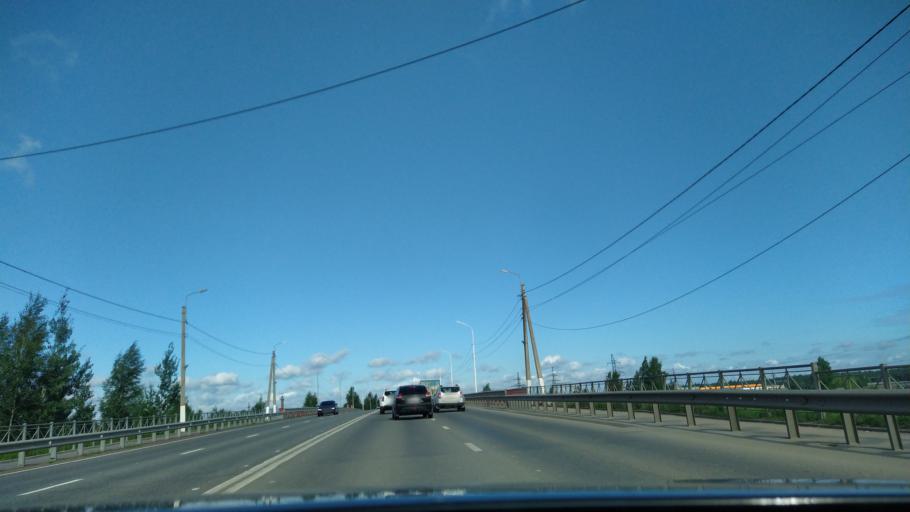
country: RU
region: Leningrad
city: Tosno
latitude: 59.5506
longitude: 30.8593
